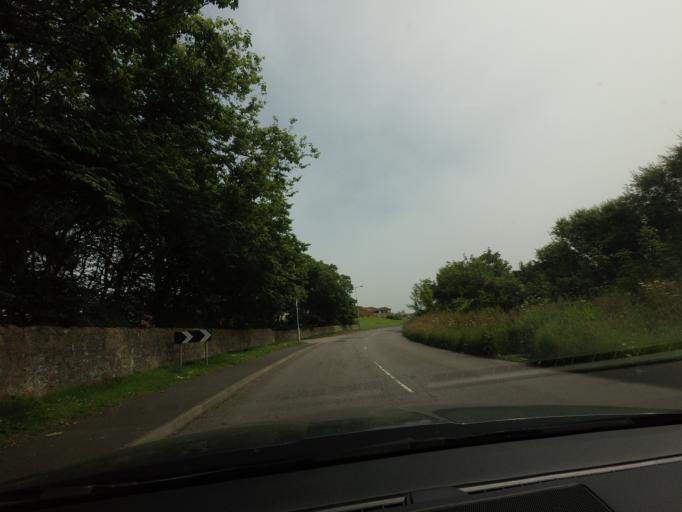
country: GB
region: Scotland
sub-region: Aberdeenshire
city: Peterhead
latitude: 57.4884
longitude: -1.7977
